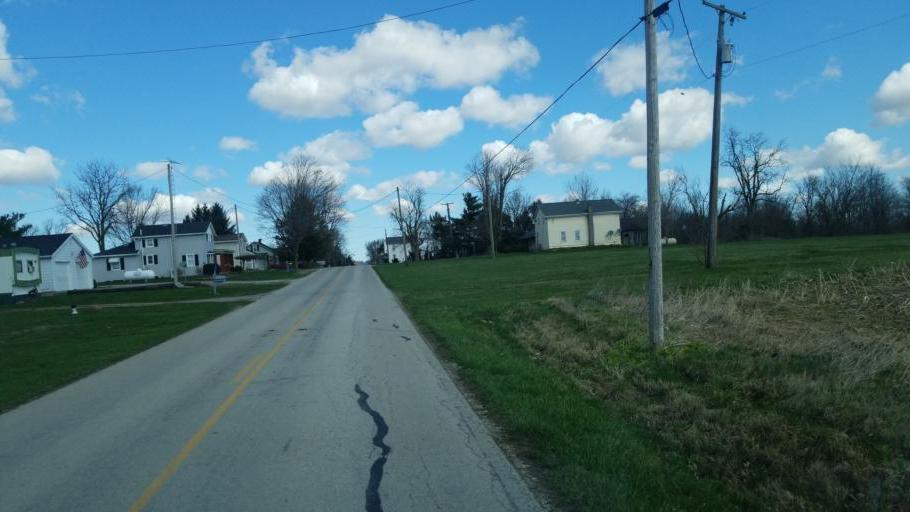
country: US
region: Ohio
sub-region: Sandusky County
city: Mount Carmel
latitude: 41.1627
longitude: -82.9381
